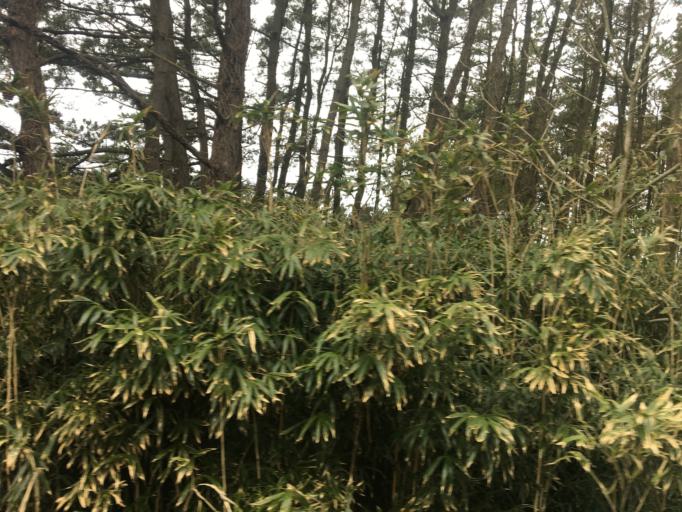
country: JP
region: Akita
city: Noshiromachi
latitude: 40.5521
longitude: 139.9418
